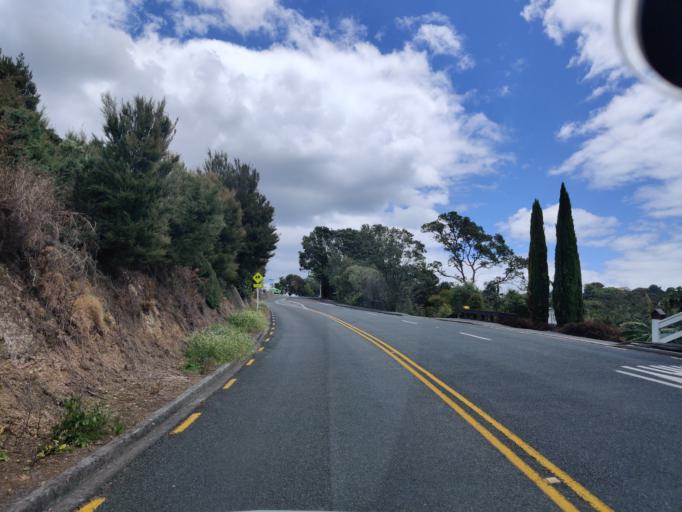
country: NZ
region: Northland
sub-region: Far North District
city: Paihia
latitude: -35.3137
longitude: 174.1195
